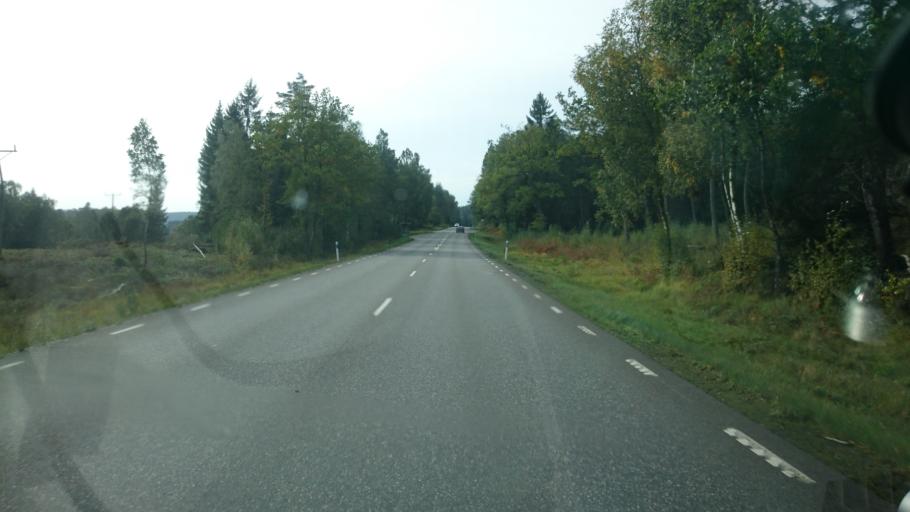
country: SE
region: Vaestra Goetaland
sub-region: Alingsas Kommun
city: Alingsas
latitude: 58.0143
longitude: 12.4510
